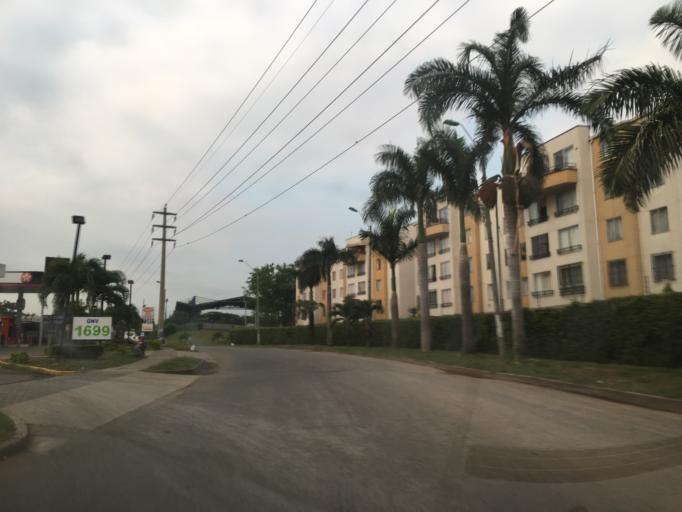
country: CO
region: Valle del Cauca
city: Cali
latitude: 3.4054
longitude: -76.5235
